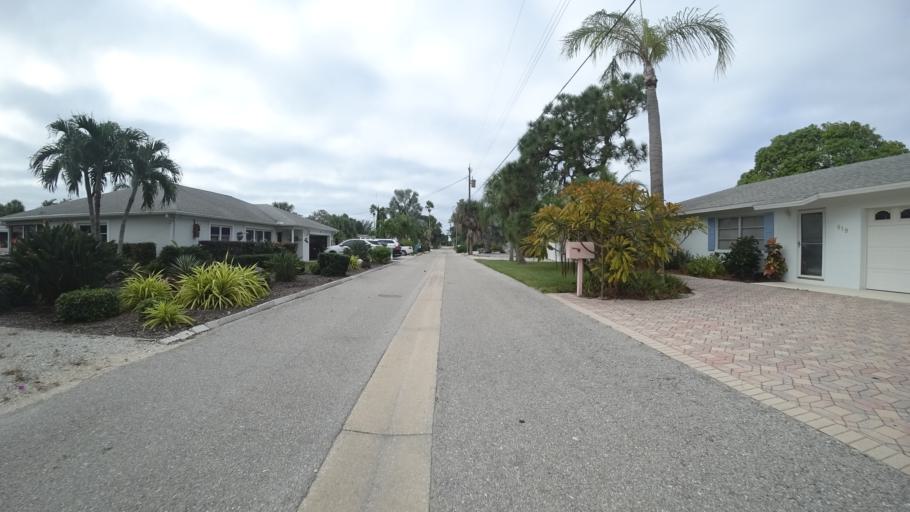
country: US
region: Florida
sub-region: Manatee County
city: Longboat Key
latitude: 27.4165
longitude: -82.6593
